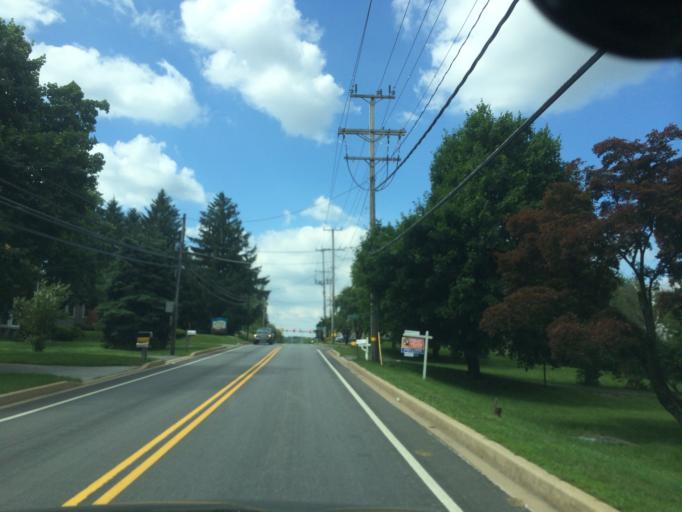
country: US
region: Maryland
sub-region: Carroll County
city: Westminster
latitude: 39.5473
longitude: -76.9923
